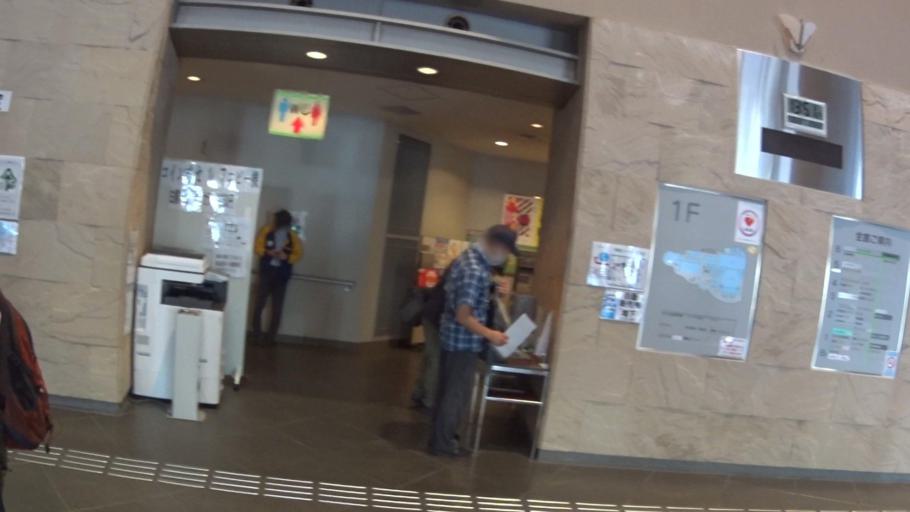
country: JP
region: Ehime
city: Kihoku-cho
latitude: 33.3684
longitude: 132.7925
